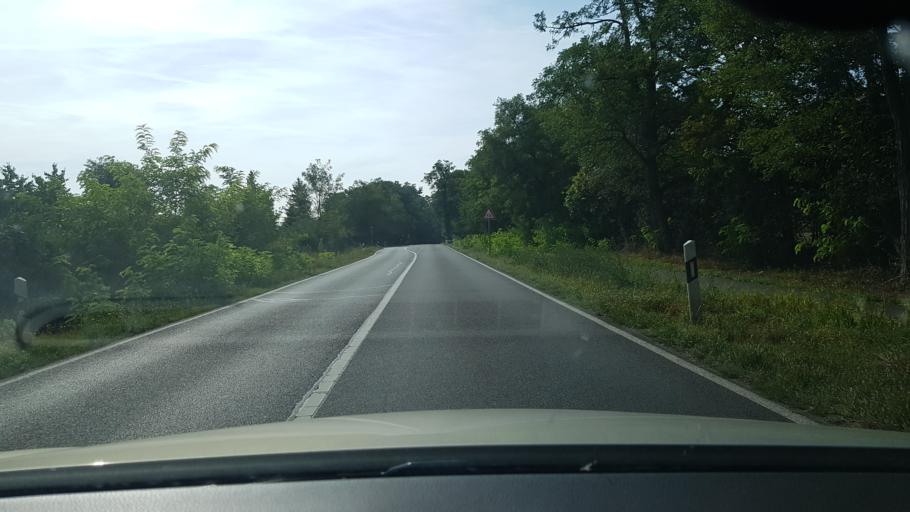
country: DE
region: Brandenburg
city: Lawitz
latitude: 52.1118
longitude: 14.6454
